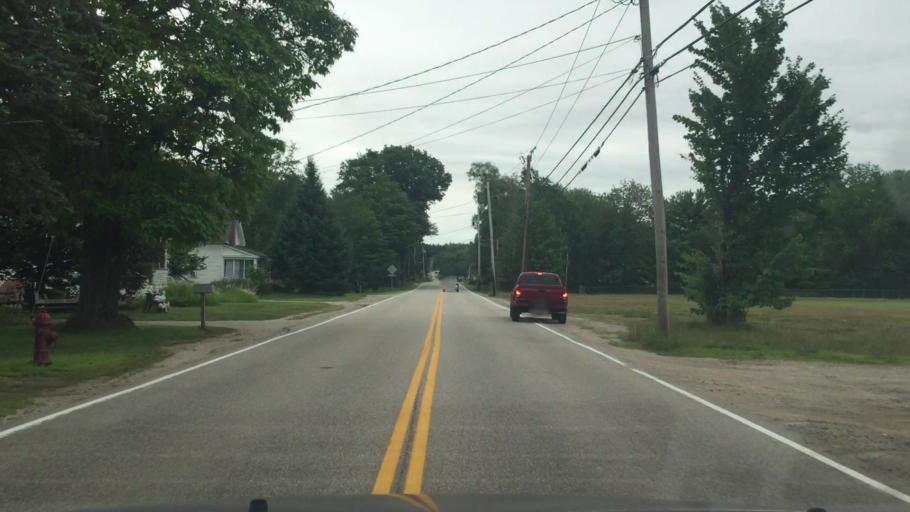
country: US
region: New Hampshire
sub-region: Carroll County
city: Conway
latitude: 43.9733
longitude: -71.1160
